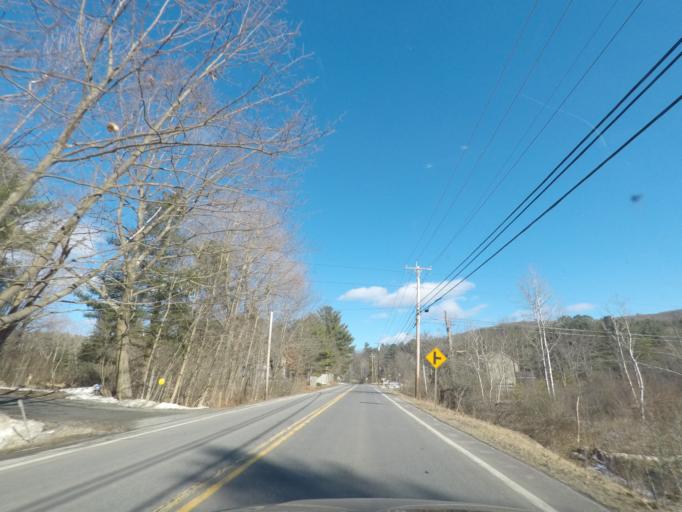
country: US
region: New York
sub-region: Columbia County
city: Chatham
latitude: 42.3185
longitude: -73.5020
